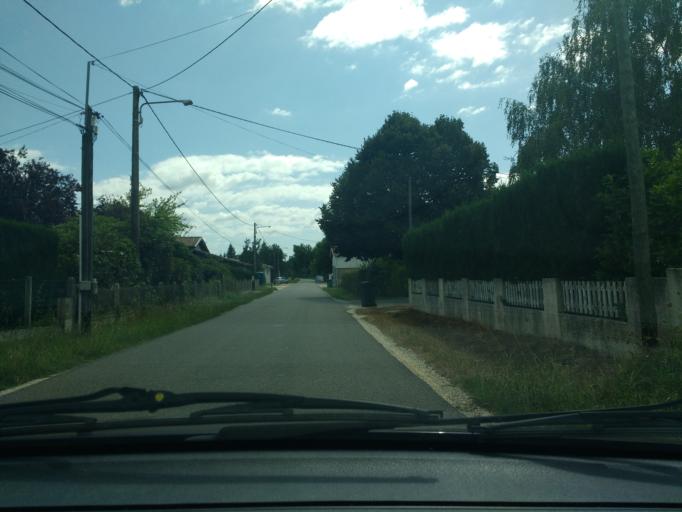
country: FR
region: Aquitaine
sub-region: Departement de la Gironde
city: Salles
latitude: 44.5596
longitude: -0.8552
